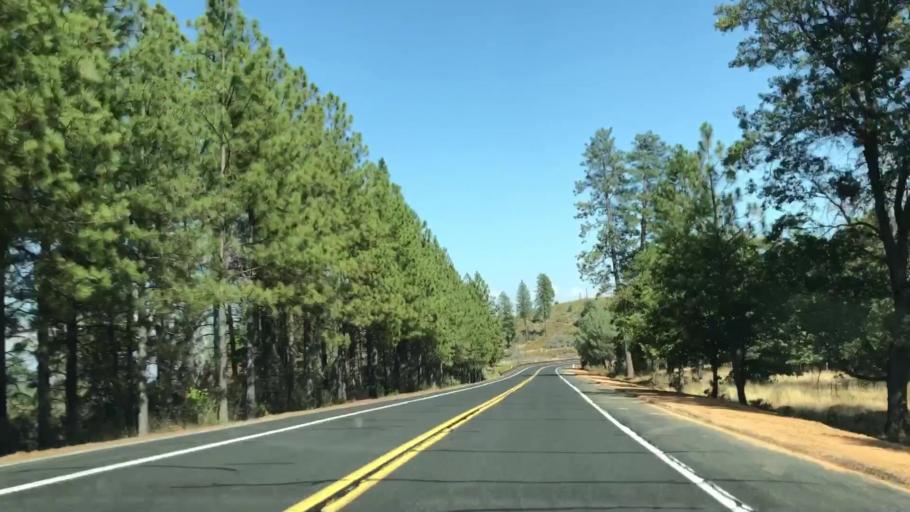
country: US
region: California
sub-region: Tuolumne County
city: Tuolumne City
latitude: 37.8252
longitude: -120.0952
